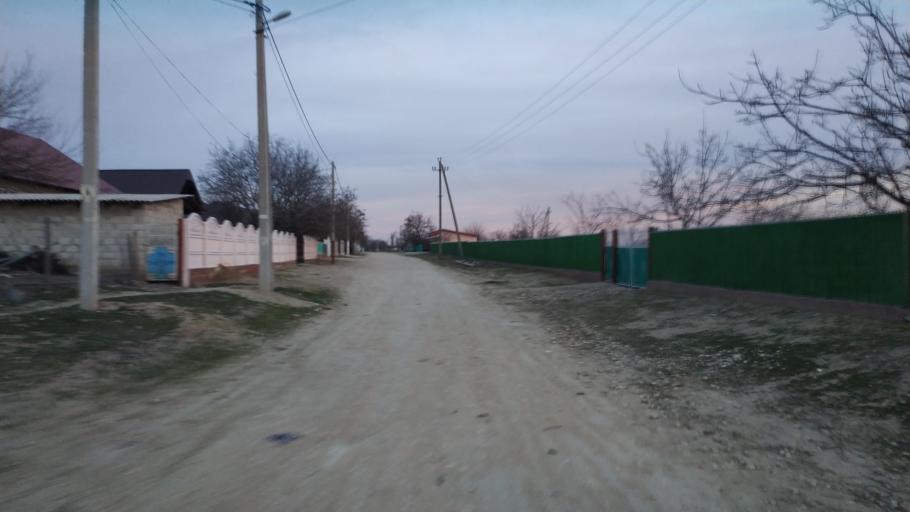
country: MD
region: Hincesti
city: Dancu
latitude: 46.7416
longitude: 28.2197
